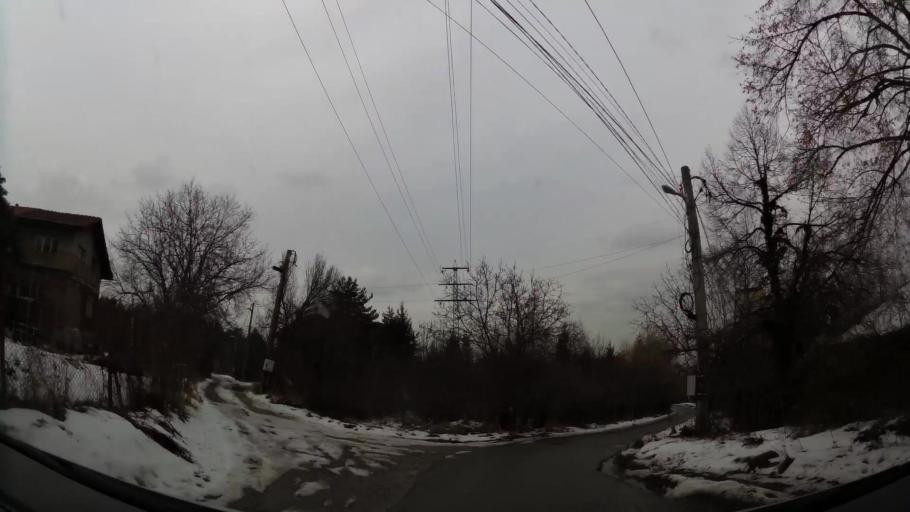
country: BG
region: Sofiya
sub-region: Obshtina Bozhurishte
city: Bozhurishte
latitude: 42.6718
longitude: 23.2276
